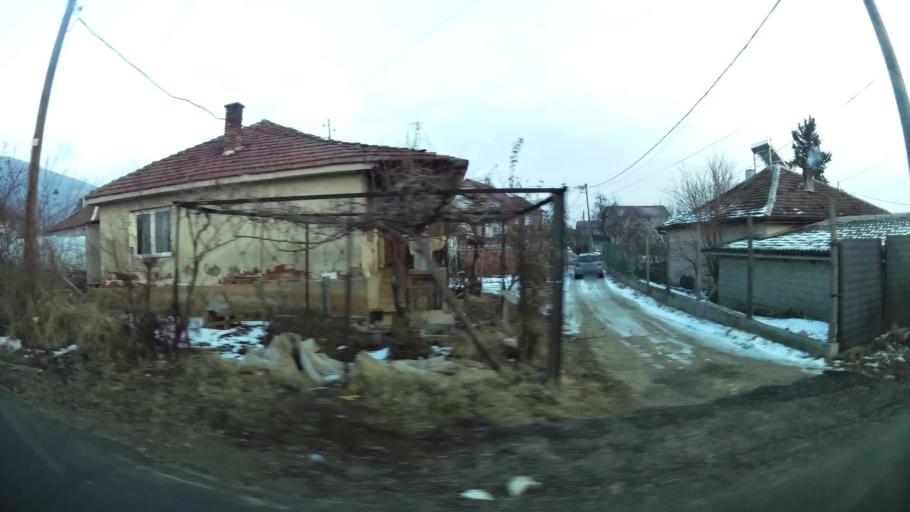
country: MK
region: Aracinovo
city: Arachinovo
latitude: 42.0324
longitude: 21.5463
